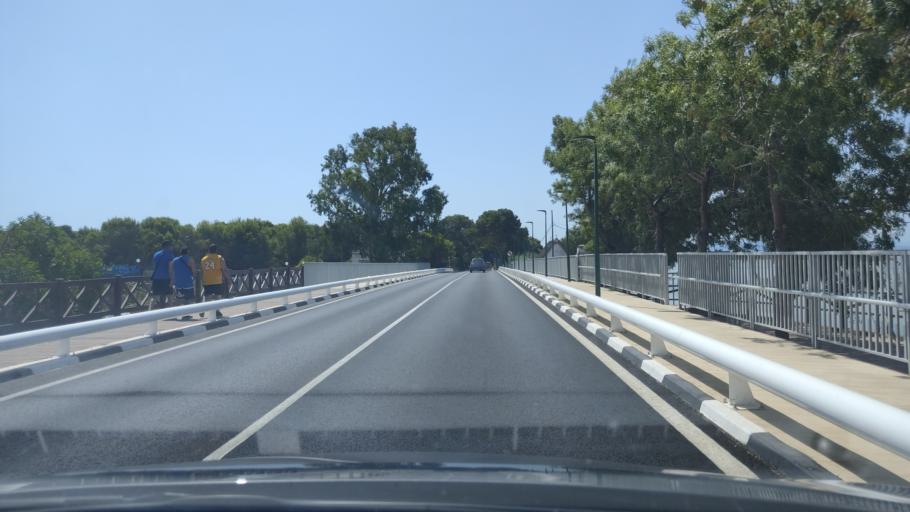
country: ES
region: Valencia
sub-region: Provincia de Valencia
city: Sollana
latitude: 39.3489
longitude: -0.3233
